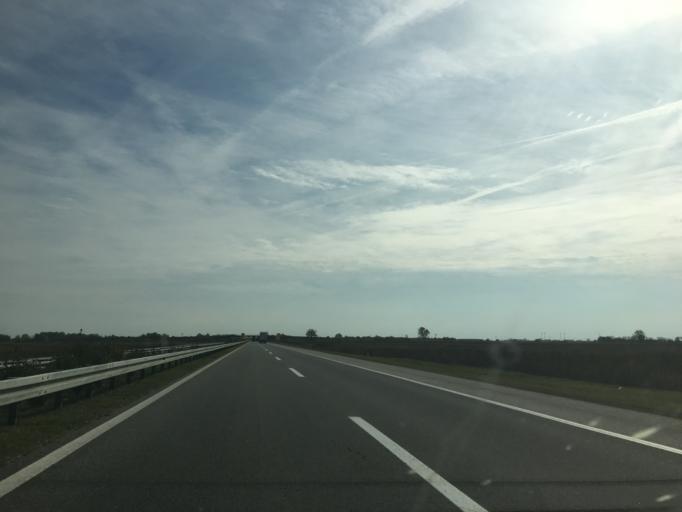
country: RS
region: Autonomna Pokrajina Vojvodina
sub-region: Sremski Okrug
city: Stara Pazova
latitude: 45.0171
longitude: 20.1953
